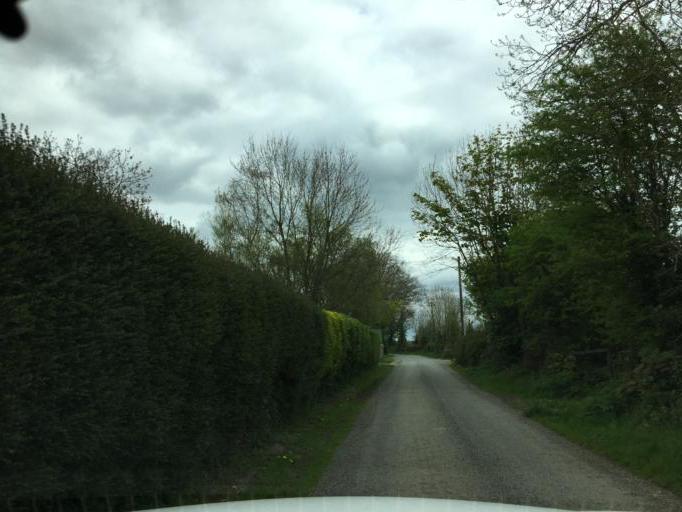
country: IE
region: Leinster
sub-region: Loch Garman
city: New Ross
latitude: 52.4308
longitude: -6.9918
